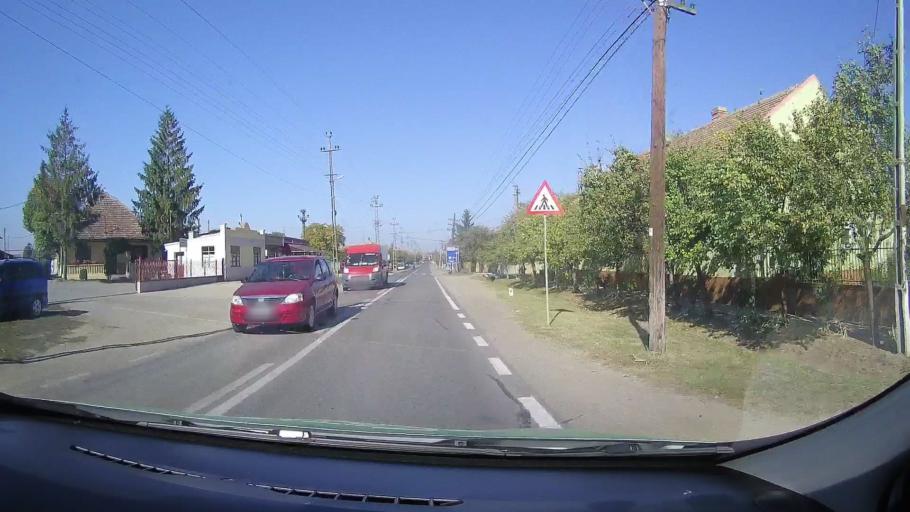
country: RO
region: Satu Mare
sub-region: Comuna Urziceni
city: Urziceni
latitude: 47.7302
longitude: 22.4055
